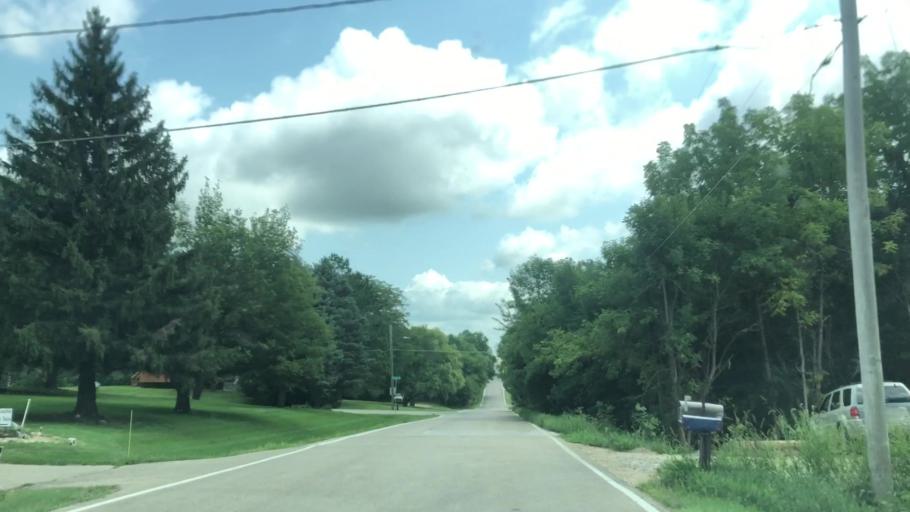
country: US
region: Iowa
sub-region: Marshall County
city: Marshalltown
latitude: 42.0287
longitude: -92.9408
